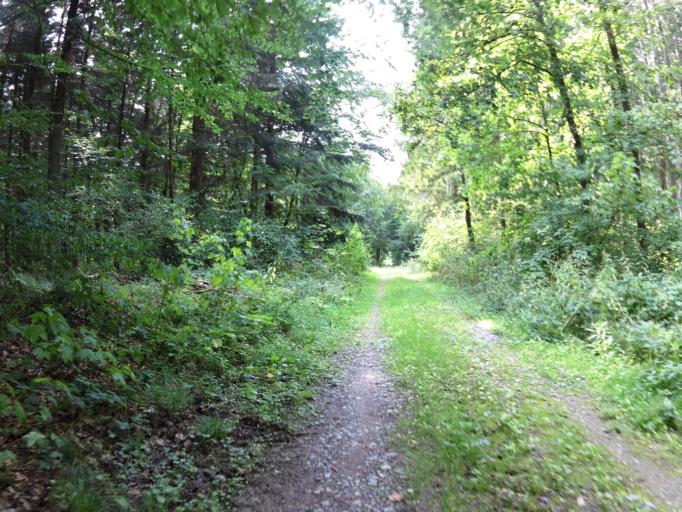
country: DE
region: Bavaria
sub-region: Regierungsbezirk Unterfranken
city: Kleinrinderfeld
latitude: 49.7040
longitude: 9.8097
